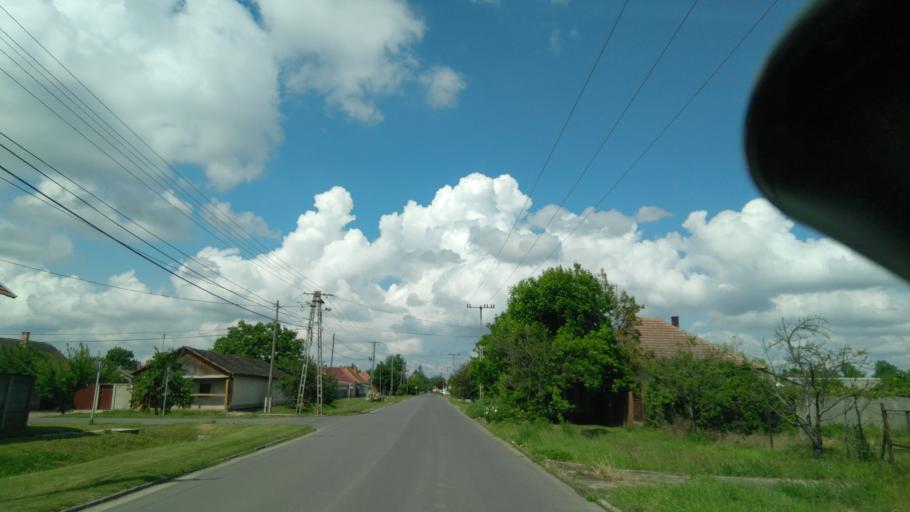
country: HU
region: Bekes
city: Mezobereny
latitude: 46.8349
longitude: 21.0255
